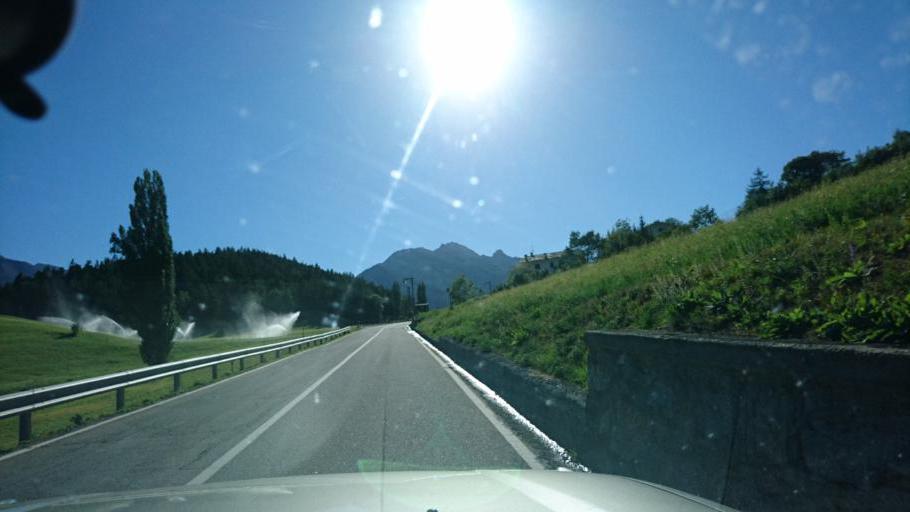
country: IT
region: Aosta Valley
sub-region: Valle d'Aosta
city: Saint-Nicolas
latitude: 45.7154
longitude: 7.1714
